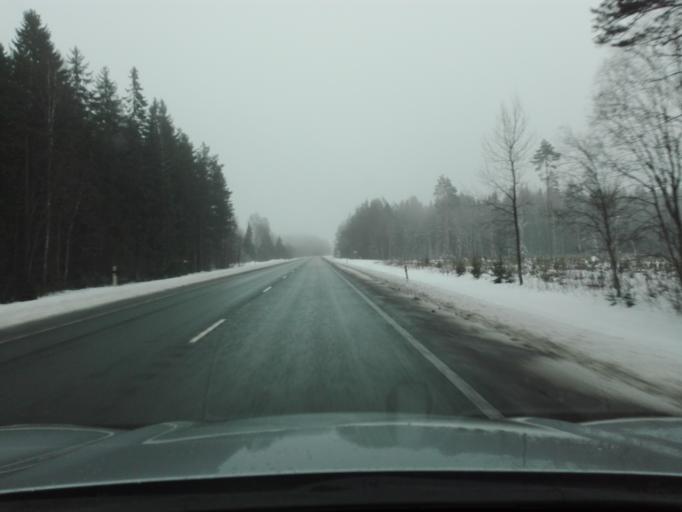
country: EE
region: Raplamaa
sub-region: Kohila vald
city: Kohila
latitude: 59.1459
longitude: 24.7859
